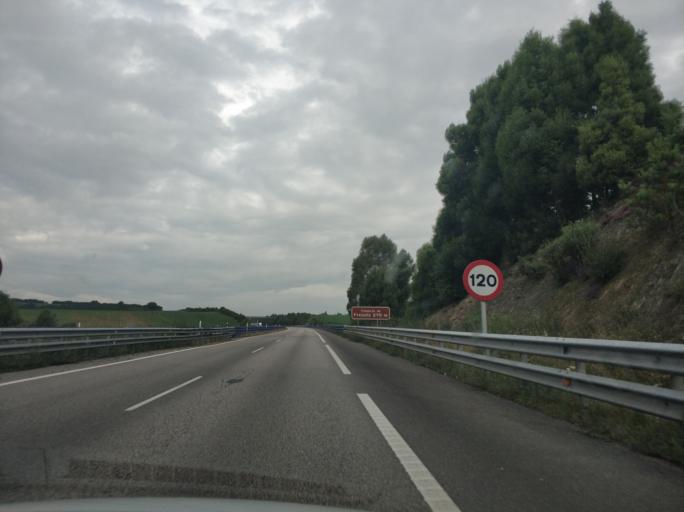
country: ES
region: Asturias
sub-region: Province of Asturias
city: Navia
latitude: 43.5335
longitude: -6.6629
